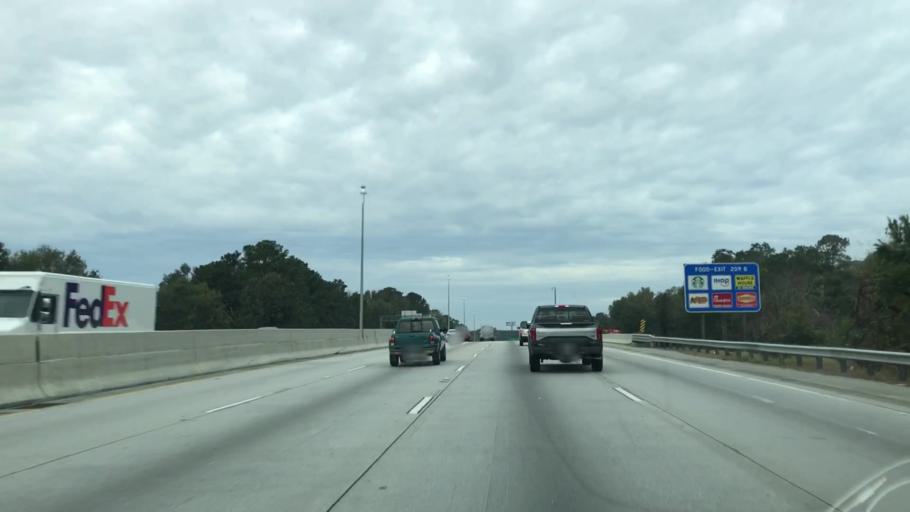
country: US
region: South Carolina
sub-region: Berkeley County
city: Hanahan
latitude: 32.9200
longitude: -80.0366
